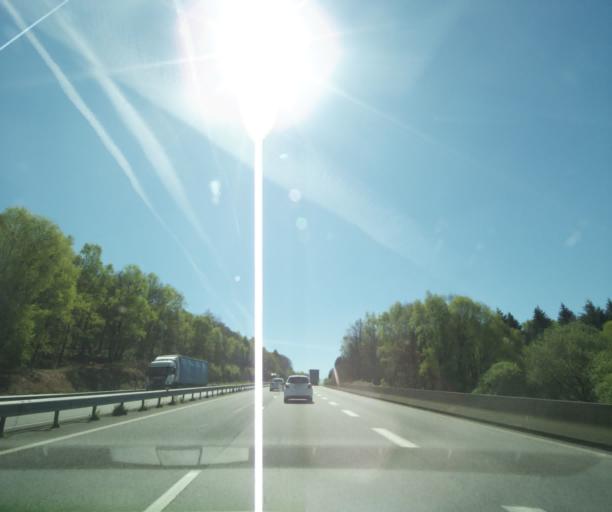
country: FR
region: Limousin
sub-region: Departement de la Haute-Vienne
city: Bessines-sur-Gartempe
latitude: 46.0675
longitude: 1.3609
